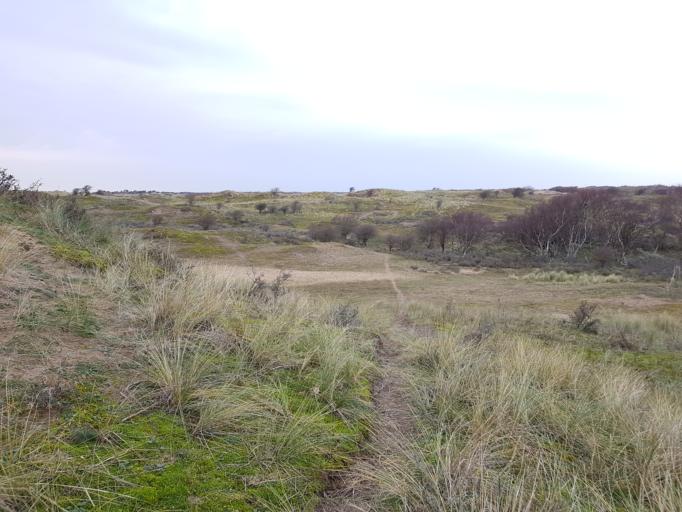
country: NL
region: South Holland
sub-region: Gemeente Noordwijkerhout
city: Noordwijkerhout
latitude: 52.2994
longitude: 4.5027
